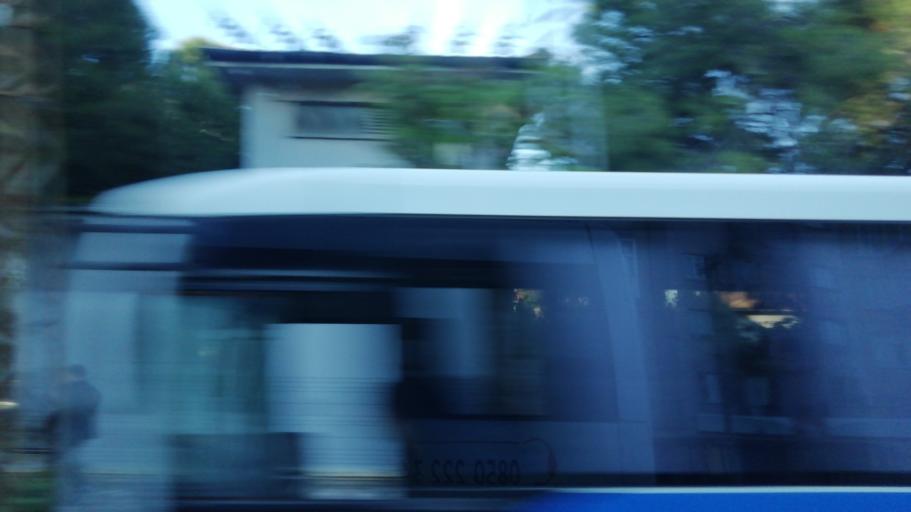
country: TR
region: Manisa
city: Akhisar
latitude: 38.9270
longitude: 27.8345
